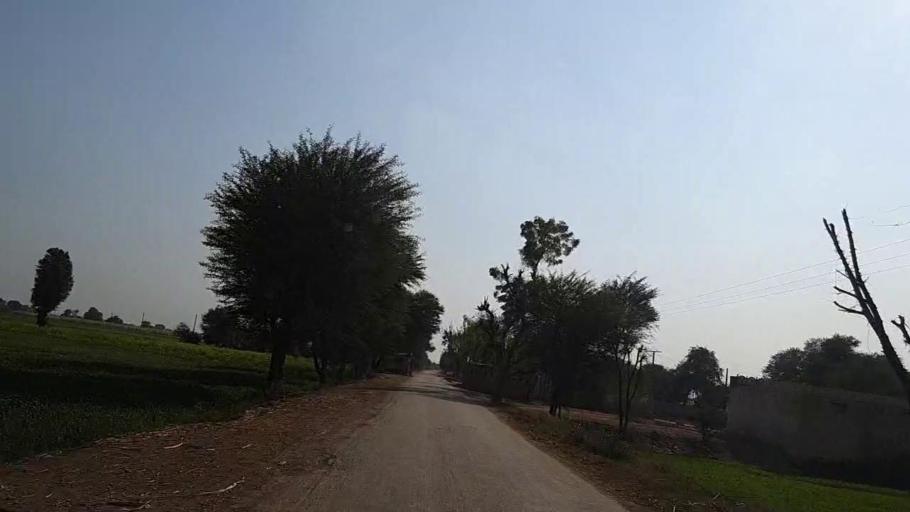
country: PK
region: Sindh
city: Sakrand
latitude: 26.0632
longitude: 68.2895
